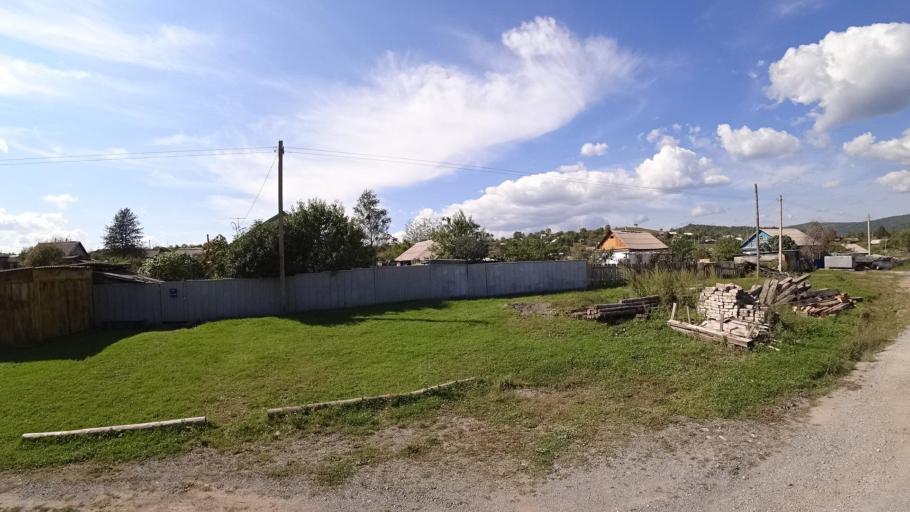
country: RU
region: Jewish Autonomous Oblast
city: Londoko
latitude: 49.0087
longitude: 131.8719
